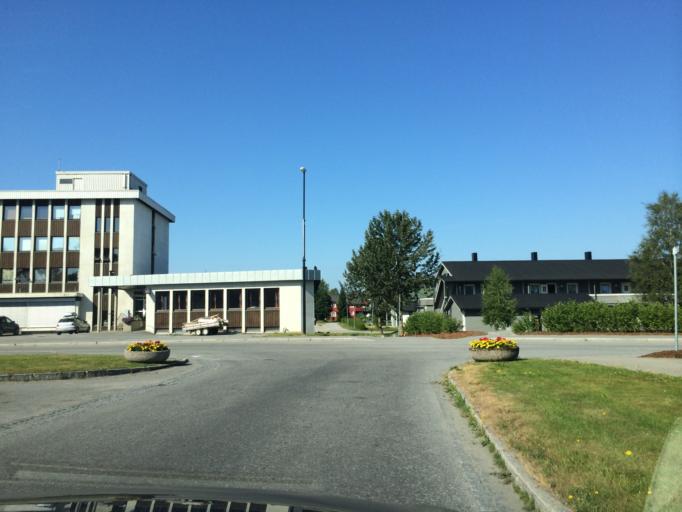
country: NO
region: Nord-Trondelag
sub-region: Overhalla
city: Ranemsletta
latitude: 64.4943
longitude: 11.9486
